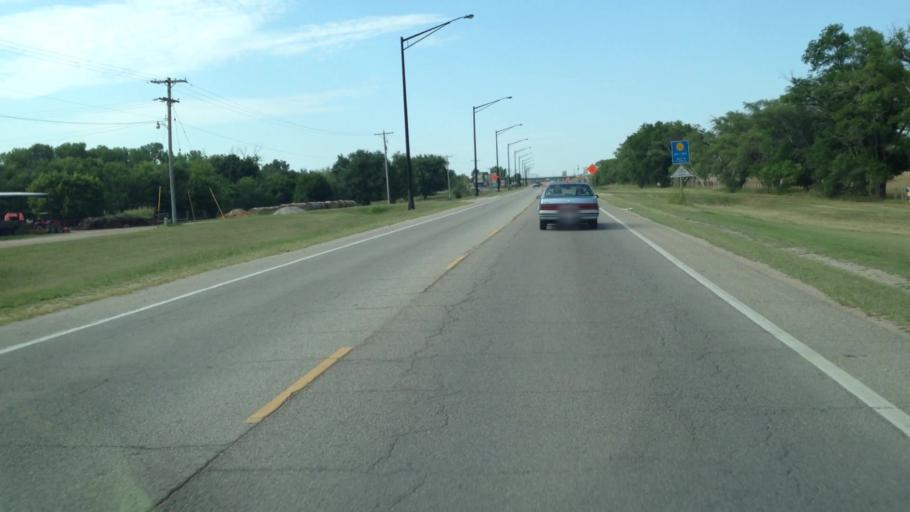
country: US
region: Kansas
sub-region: Labette County
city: Parsons
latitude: 37.3574
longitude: -95.2587
